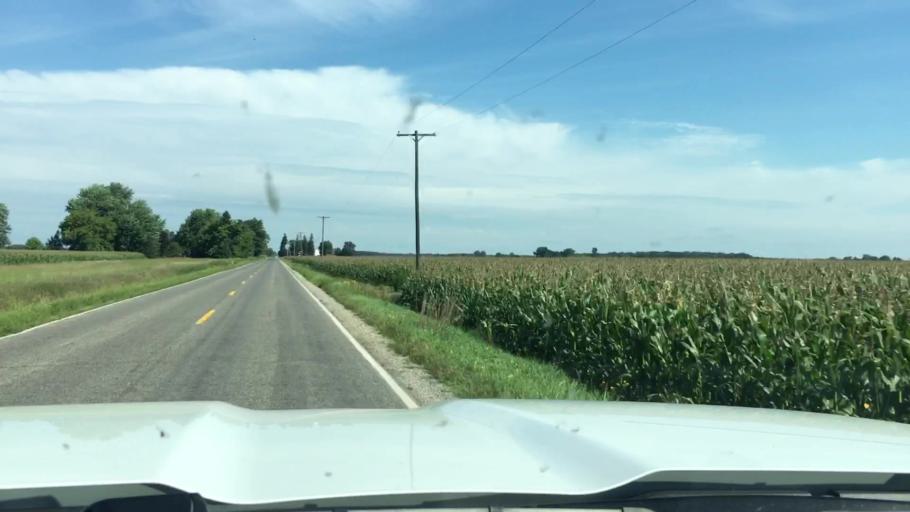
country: US
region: Michigan
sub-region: Saginaw County
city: Hemlock
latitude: 43.5113
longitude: -84.2296
